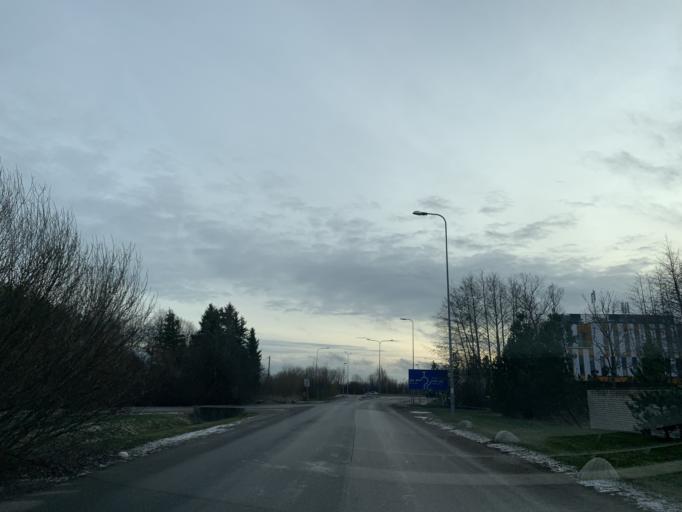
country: EE
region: Harju
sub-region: Harku vald
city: Tabasalu
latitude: 59.4383
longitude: 24.5721
